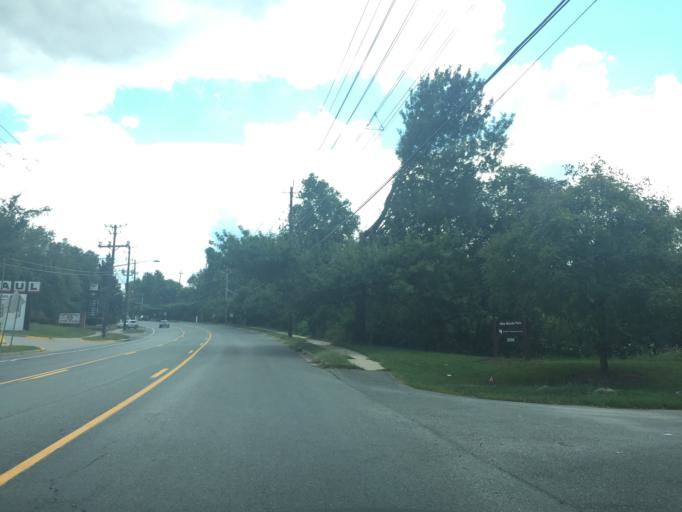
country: US
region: Maryland
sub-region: Montgomery County
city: Montgomery Village
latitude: 39.1683
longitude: -77.1752
